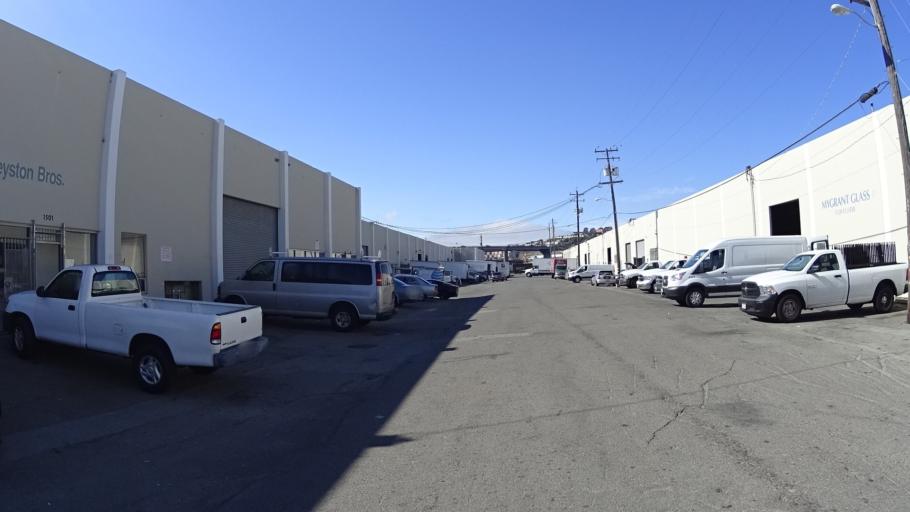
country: US
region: California
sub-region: San Francisco County
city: San Francisco
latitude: 37.7454
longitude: -122.3894
